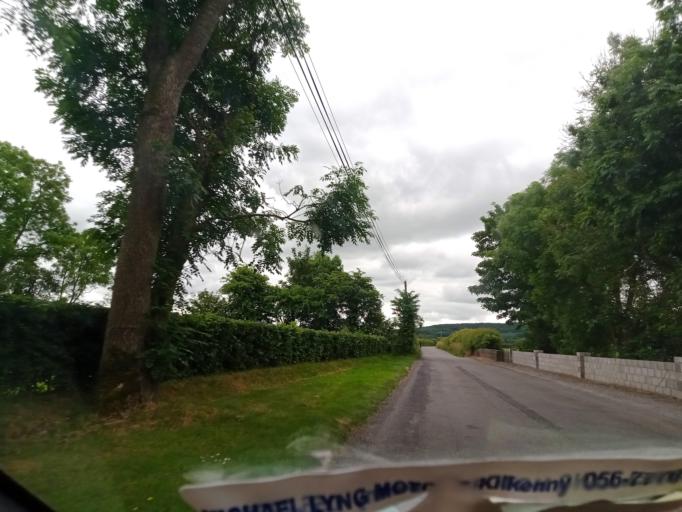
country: IE
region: Leinster
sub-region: Kilkenny
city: Ballyragget
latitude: 52.7406
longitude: -7.4165
